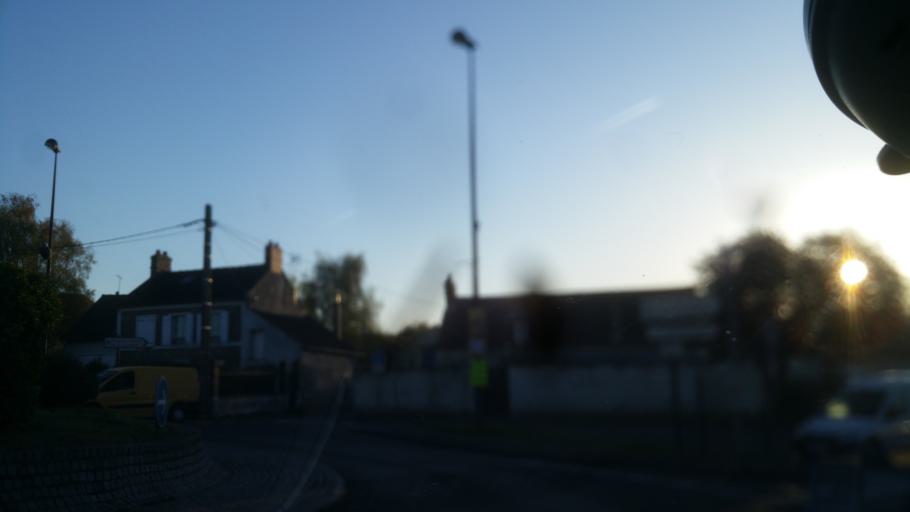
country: FR
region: Ile-de-France
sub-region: Departement de l'Essonne
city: Angervilliers
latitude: 48.5937
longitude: 2.0640
